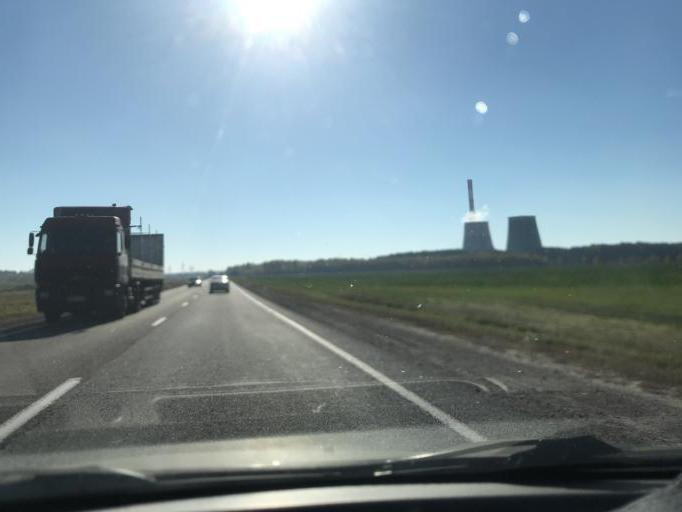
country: BY
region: Gomel
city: Kastsyukowka
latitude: 52.4600
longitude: 30.8246
